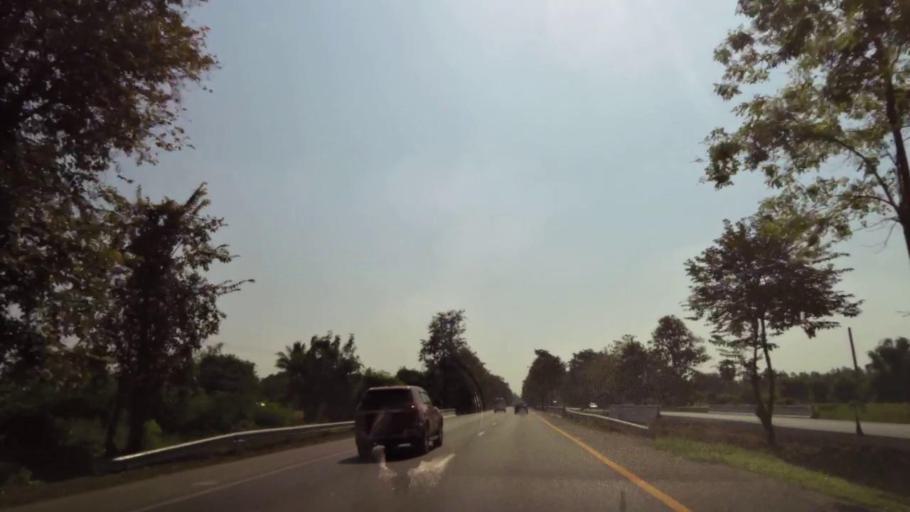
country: TH
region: Phichit
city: Bueng Na Rang
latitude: 16.0733
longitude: 100.1240
